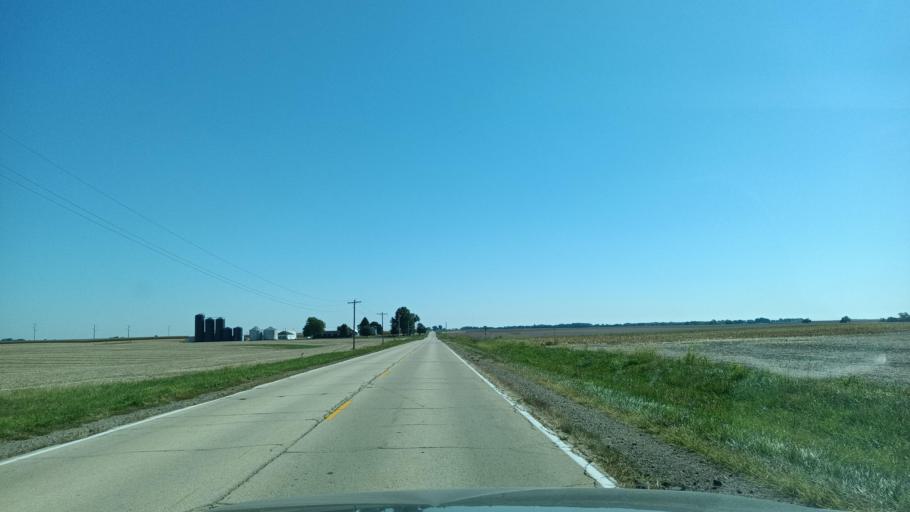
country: US
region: Illinois
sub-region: Peoria County
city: Elmwood
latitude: 40.9021
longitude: -89.9591
